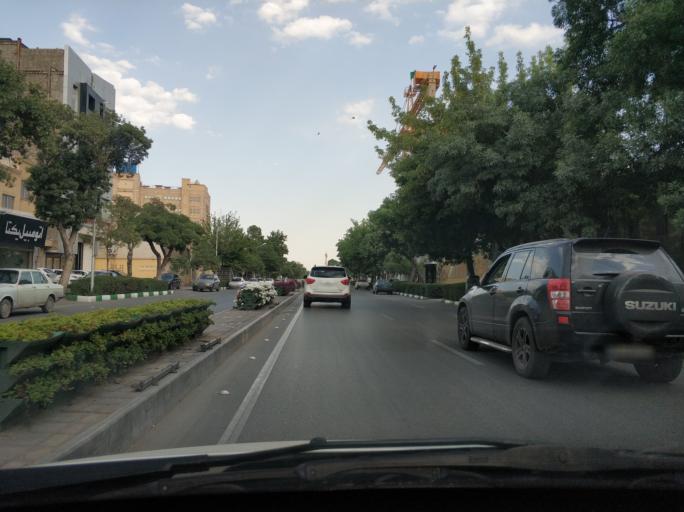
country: IR
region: Razavi Khorasan
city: Mashhad
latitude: 36.2790
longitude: 59.5980
